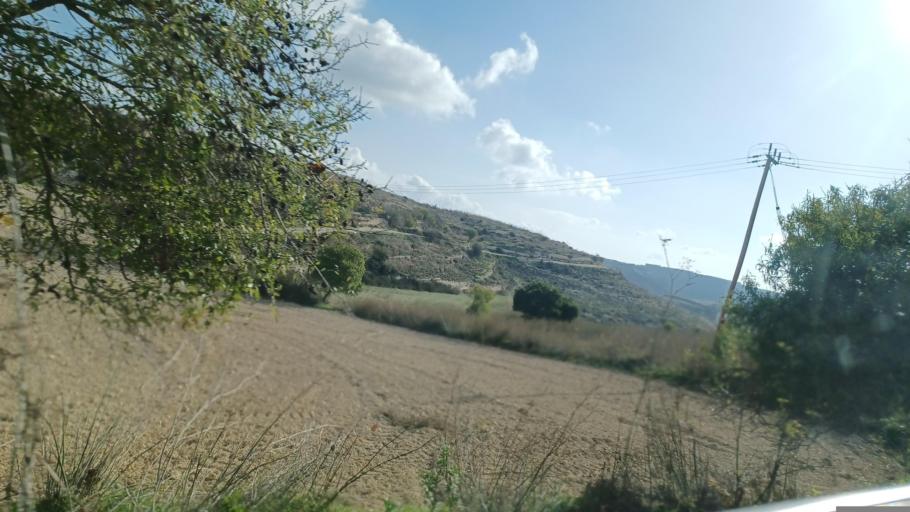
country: CY
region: Pafos
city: Mesogi
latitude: 34.8247
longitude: 32.4807
